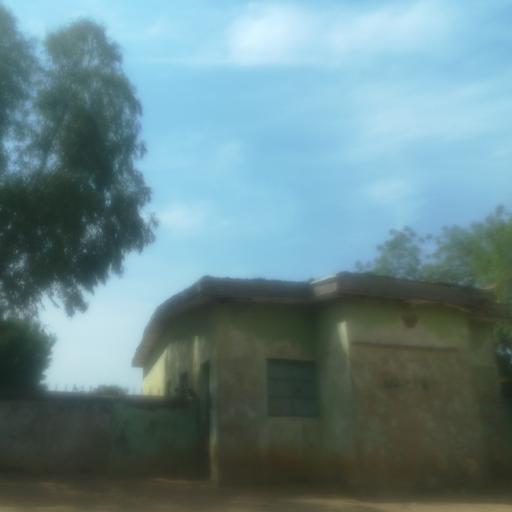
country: NG
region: Kano
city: Kano
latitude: 12.0223
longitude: 8.5204
